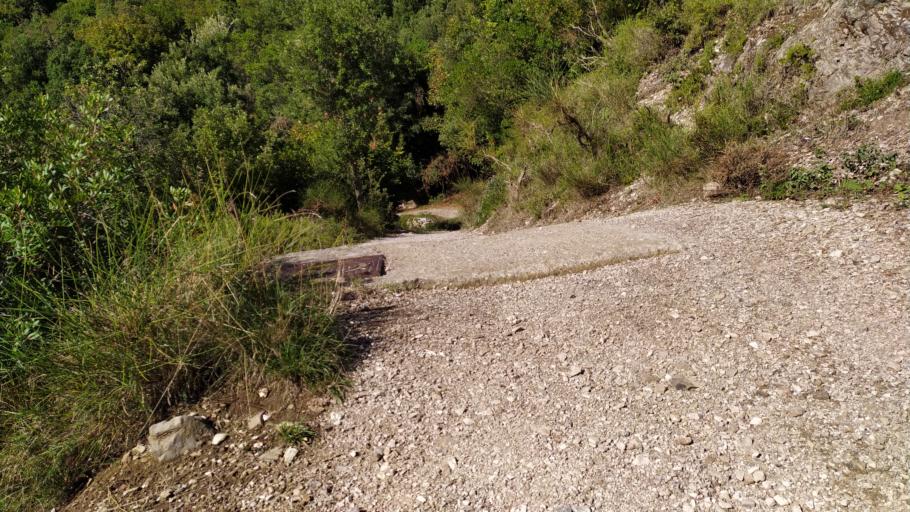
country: IT
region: Campania
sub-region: Provincia di Salerno
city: Vietri sul Mare
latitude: 40.6836
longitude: 14.7361
